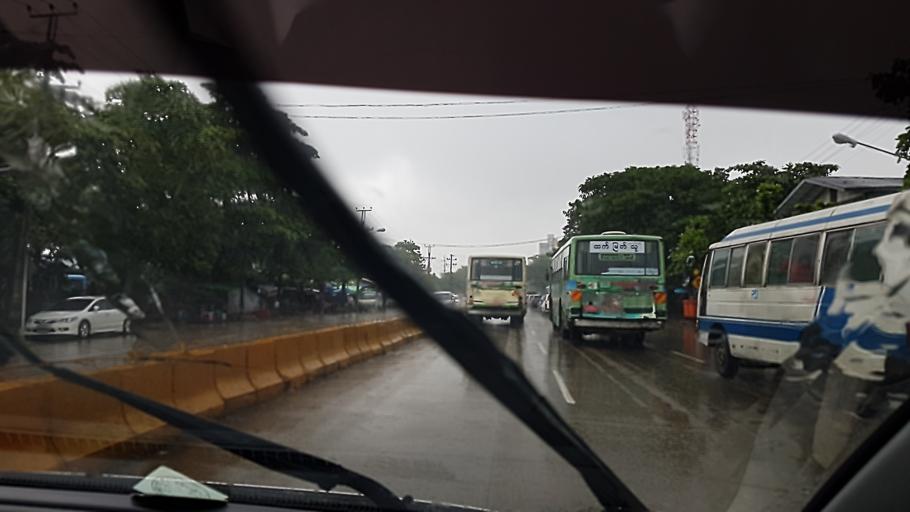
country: MM
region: Yangon
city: Yangon
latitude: 16.7814
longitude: 96.1882
